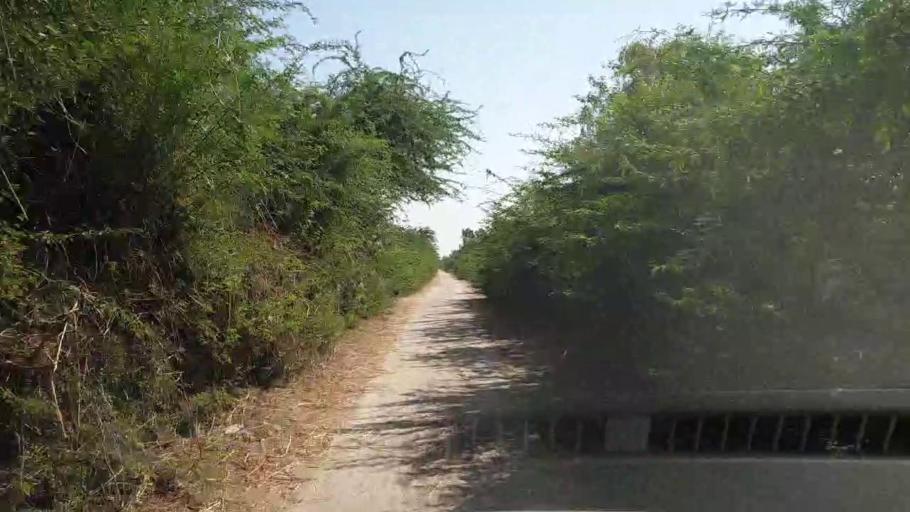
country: PK
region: Sindh
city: Tando Bago
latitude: 24.6559
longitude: 68.9806
